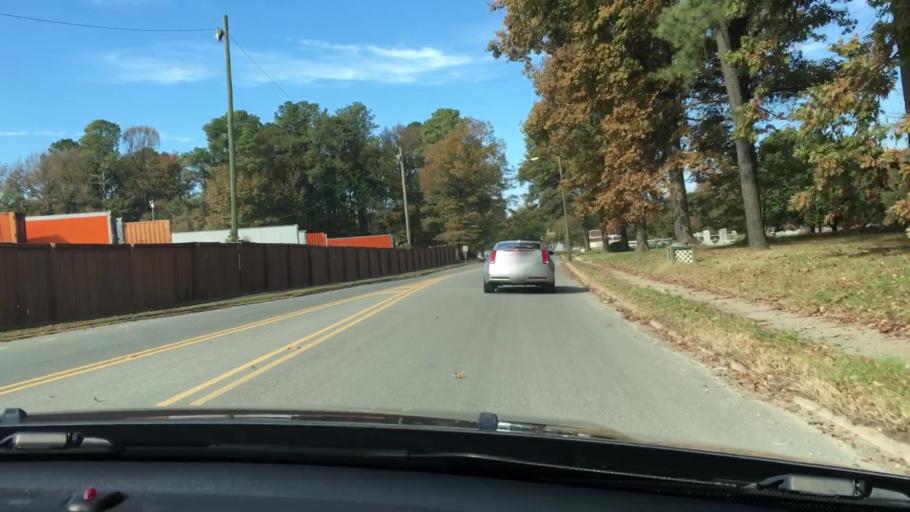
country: US
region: Virginia
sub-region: King William County
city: West Point
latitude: 37.5453
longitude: -76.8039
